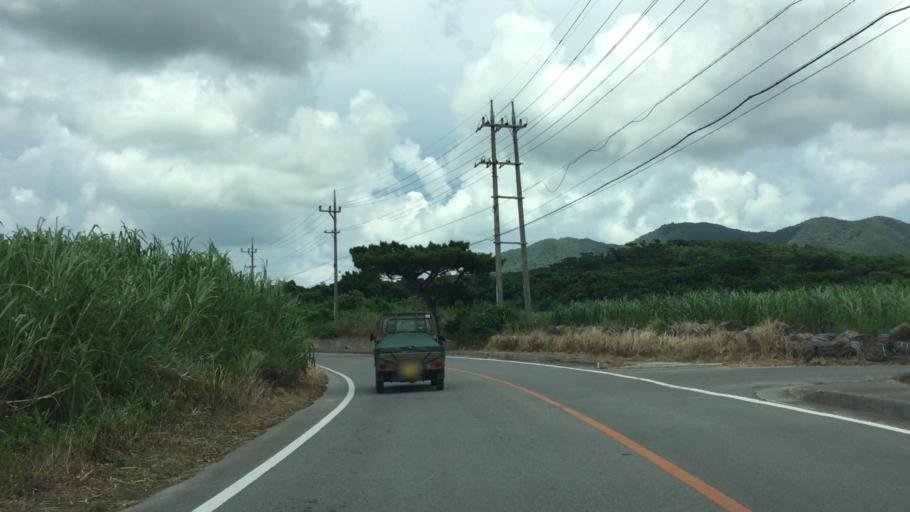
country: JP
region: Okinawa
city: Ishigaki
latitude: 24.3996
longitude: 124.1514
